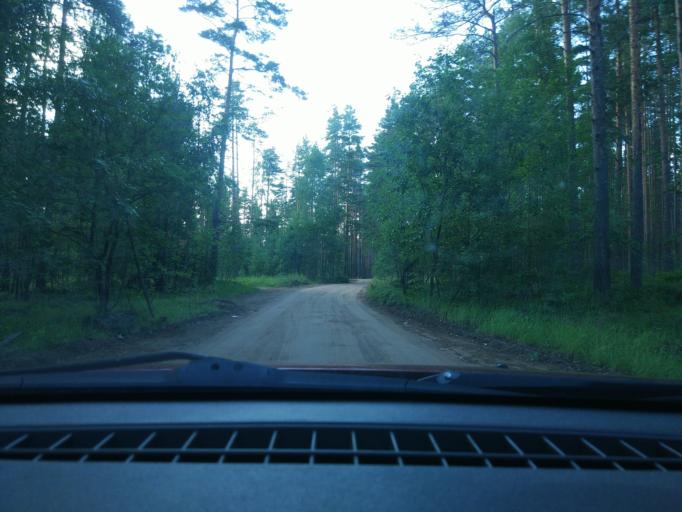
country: RU
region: Leningrad
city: Priozersk
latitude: 60.9290
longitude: 30.0545
